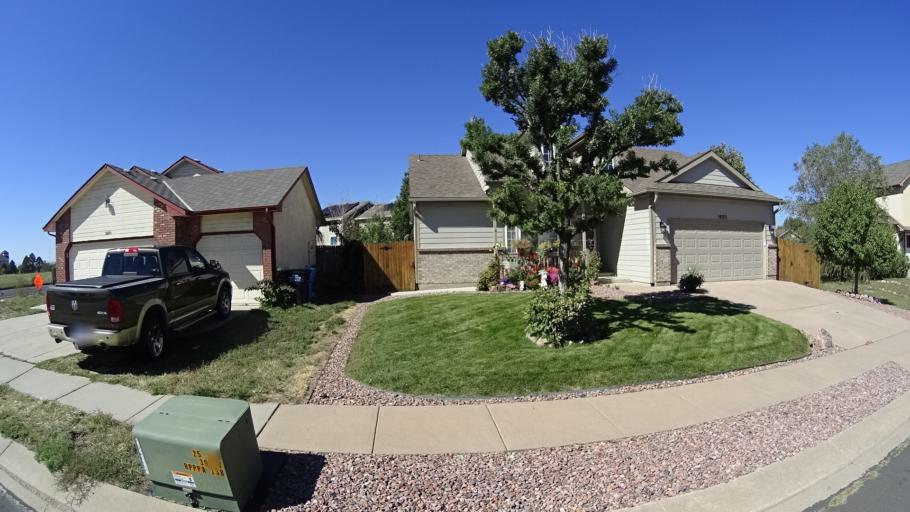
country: US
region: Colorado
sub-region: El Paso County
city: Stratmoor
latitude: 38.8088
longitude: -104.7356
